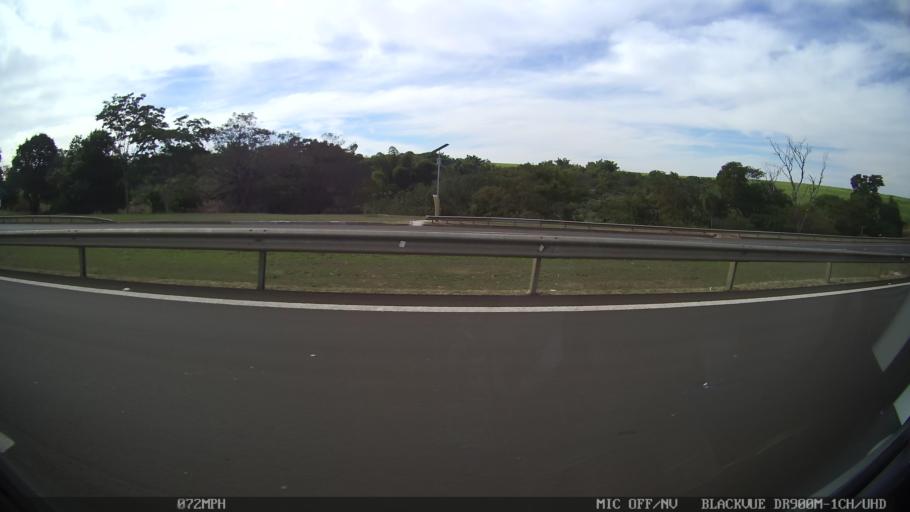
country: BR
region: Sao Paulo
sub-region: Matao
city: Matao
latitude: -21.5790
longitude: -48.4539
